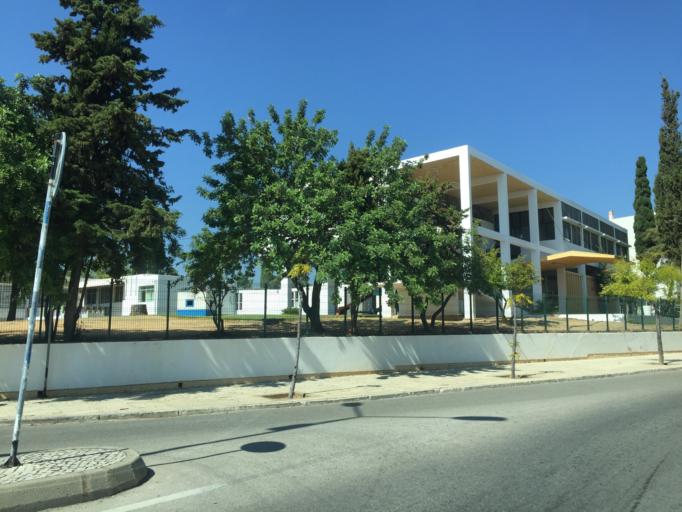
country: PT
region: Faro
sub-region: Olhao
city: Olhao
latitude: 37.0345
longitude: -7.8471
